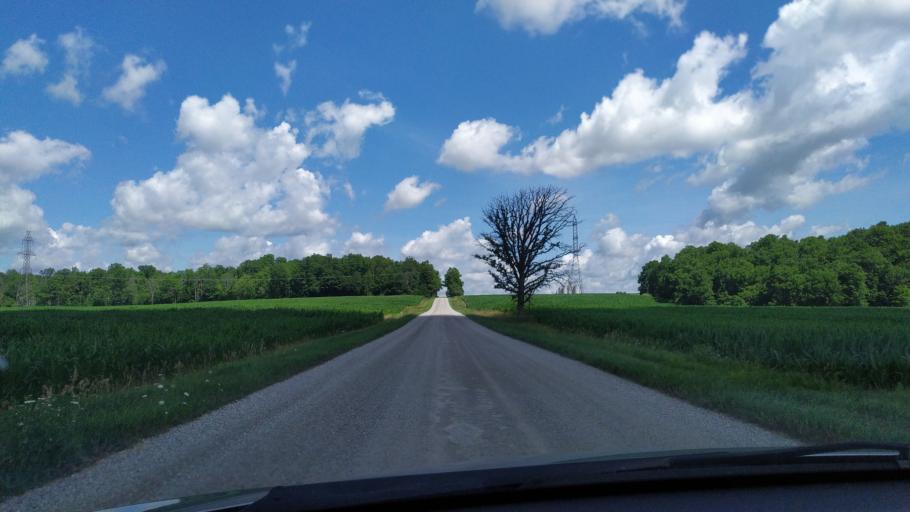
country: CA
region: Ontario
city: Stratford
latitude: 43.3751
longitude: -80.7617
